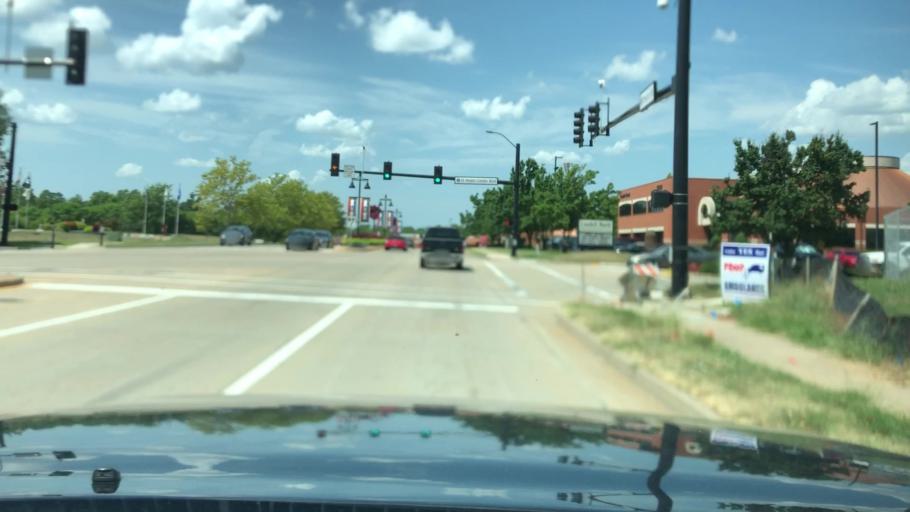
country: US
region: Missouri
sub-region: Saint Charles County
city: Saint Peters
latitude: 38.7928
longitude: -90.5953
